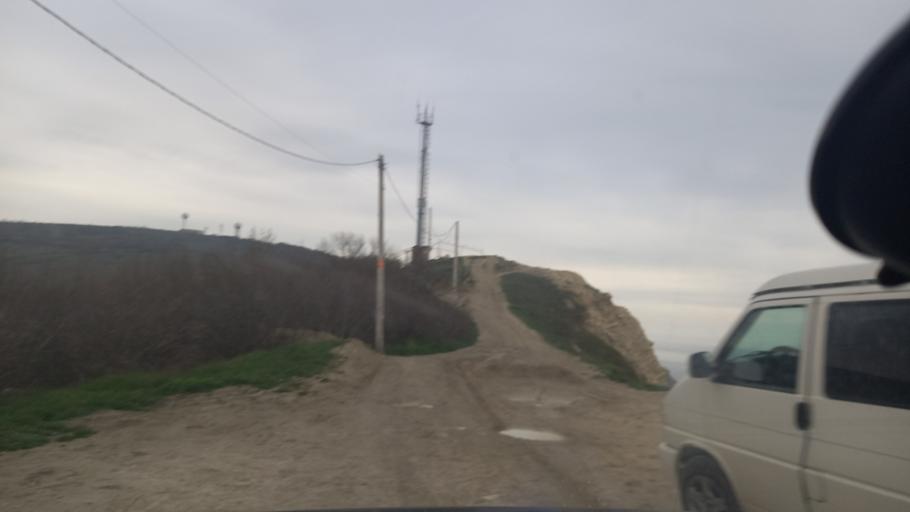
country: RU
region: Krasnodarskiy
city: Anapa
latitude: 44.8500
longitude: 37.3431
